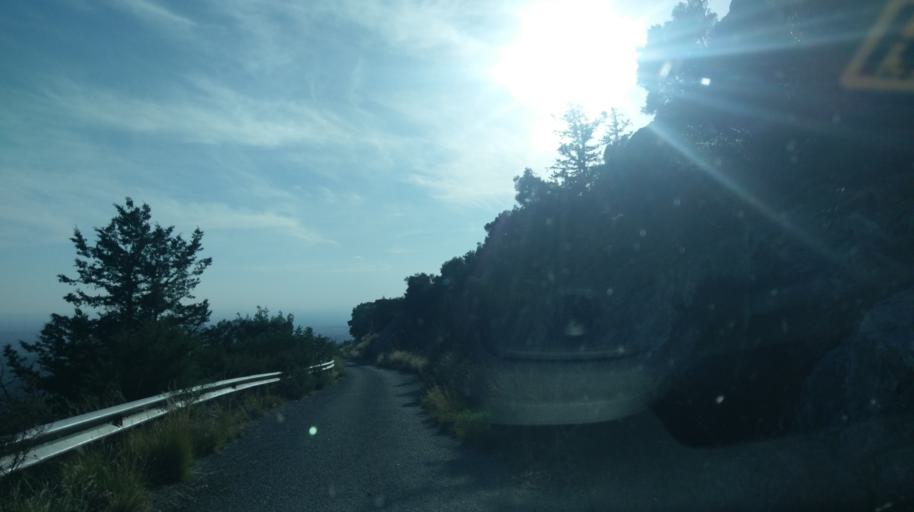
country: CY
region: Ammochostos
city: Lefkonoiko
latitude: 35.3198
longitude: 33.6216
